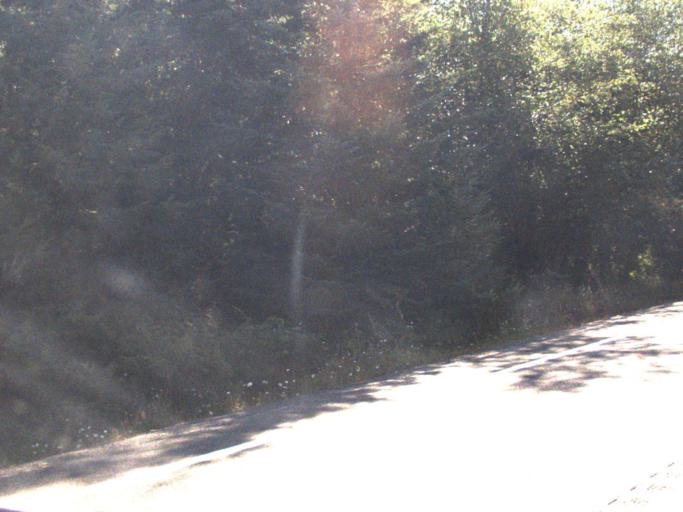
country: US
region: Washington
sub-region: King County
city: Riverbend
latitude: 47.1465
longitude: -121.6397
